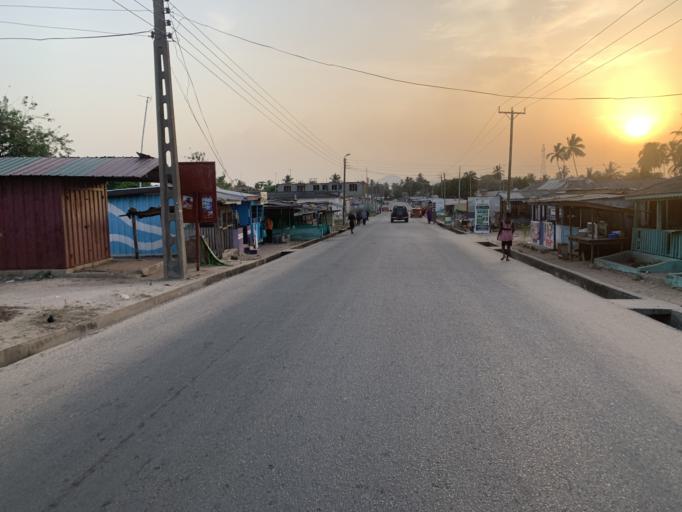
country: GH
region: Central
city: Winneba
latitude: 5.3510
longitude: -0.6220
